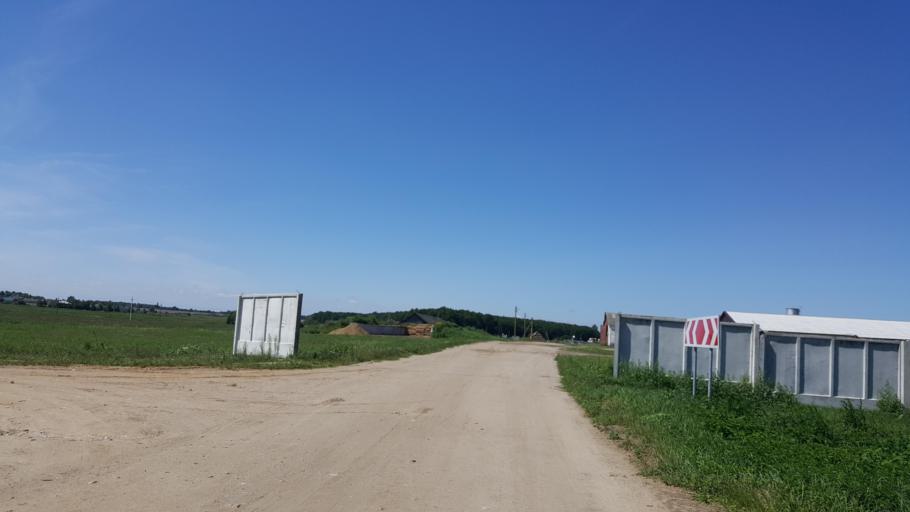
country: BY
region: Brest
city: Charnawchytsy
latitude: 52.2183
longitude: 23.7365
